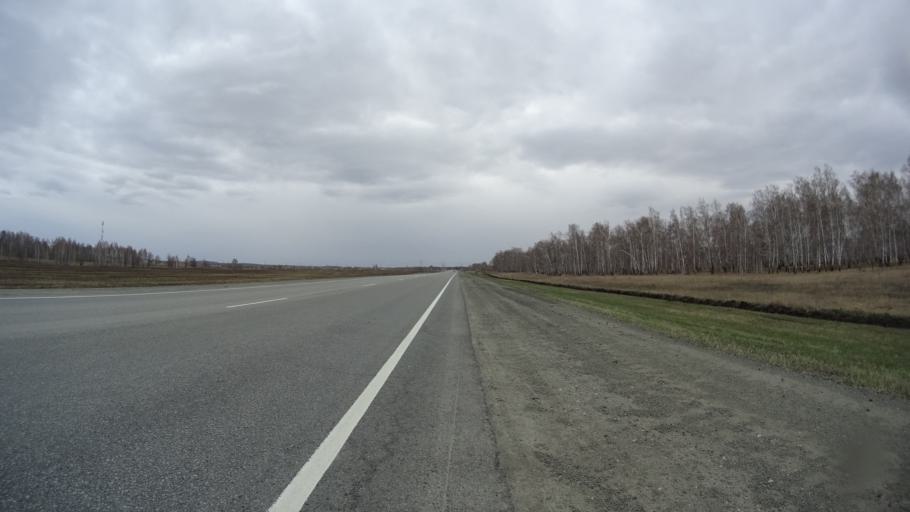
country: RU
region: Chelyabinsk
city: Krasnogorskiy
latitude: 54.6893
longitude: 61.2484
